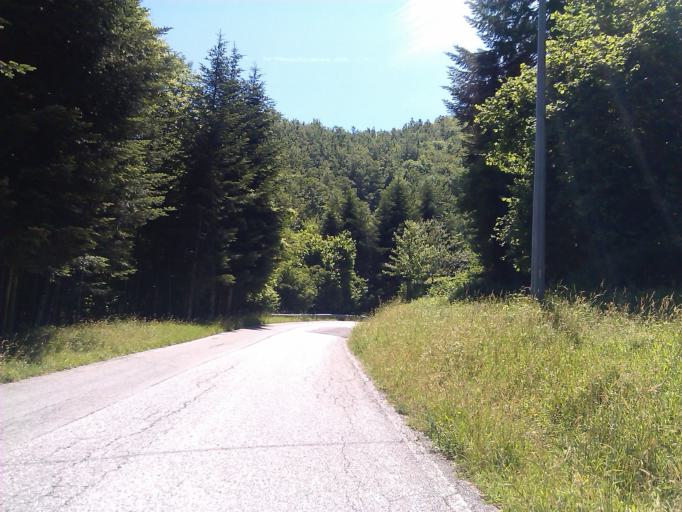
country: IT
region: Tuscany
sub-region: Provincia di Prato
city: Cantagallo
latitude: 44.0532
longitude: 11.0451
